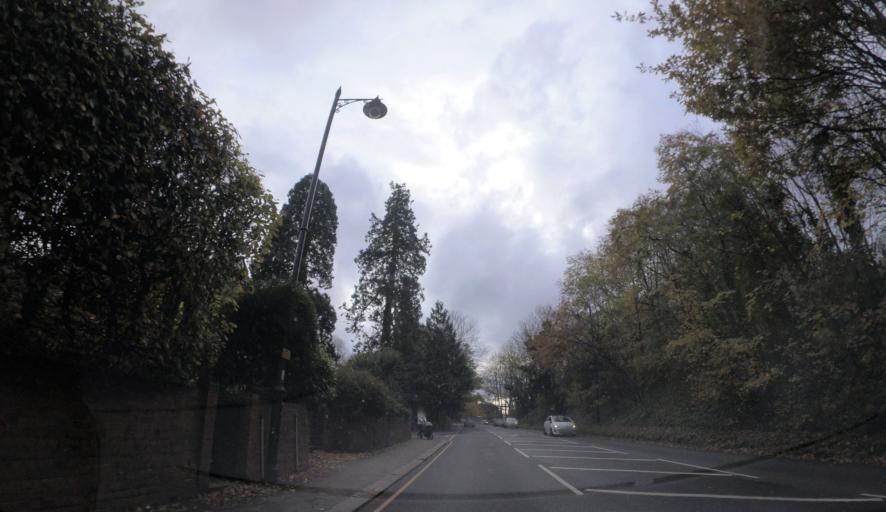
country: GB
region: England
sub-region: Surrey
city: Reigate
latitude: 51.2336
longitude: -0.2034
